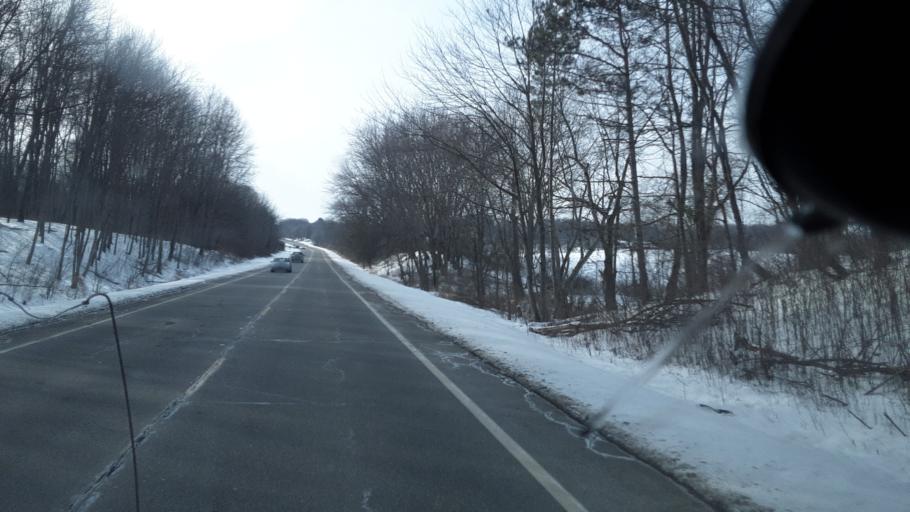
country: US
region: Ohio
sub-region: Summit County
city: Mogadore
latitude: 41.0272
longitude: -81.3388
